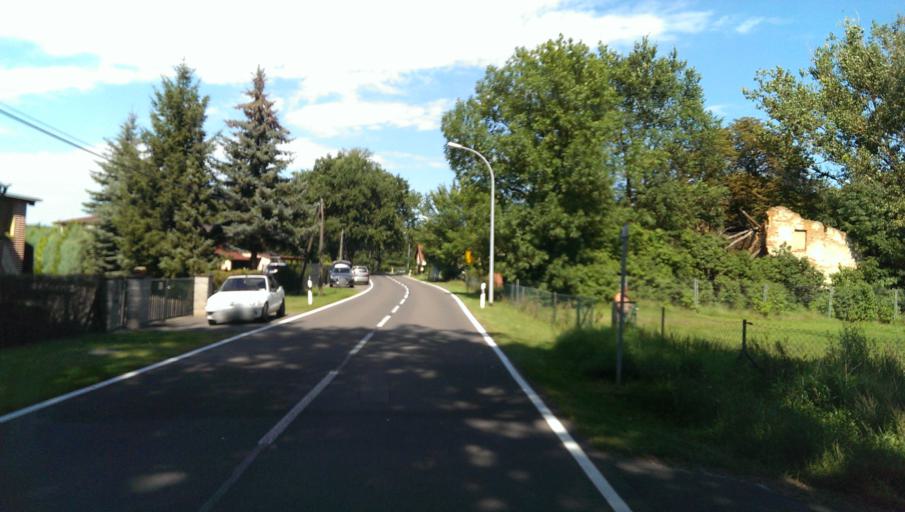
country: DE
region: Brandenburg
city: Trebbin
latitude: 52.2551
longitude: 13.2064
